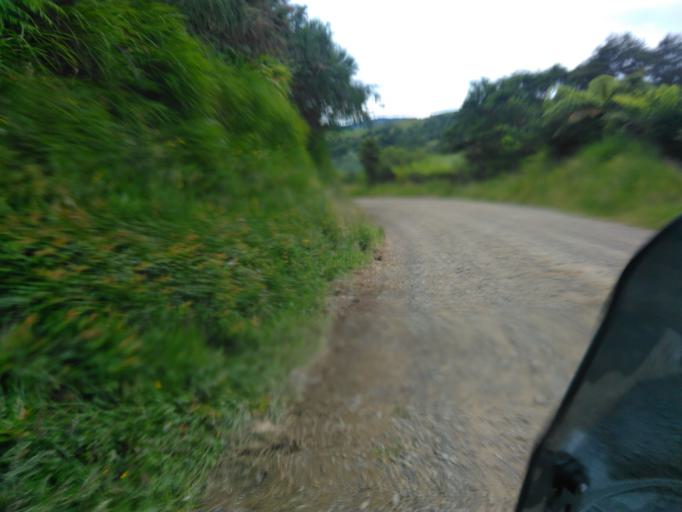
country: NZ
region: Bay of Plenty
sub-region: Opotiki District
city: Opotiki
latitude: -38.0310
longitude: 177.4412
